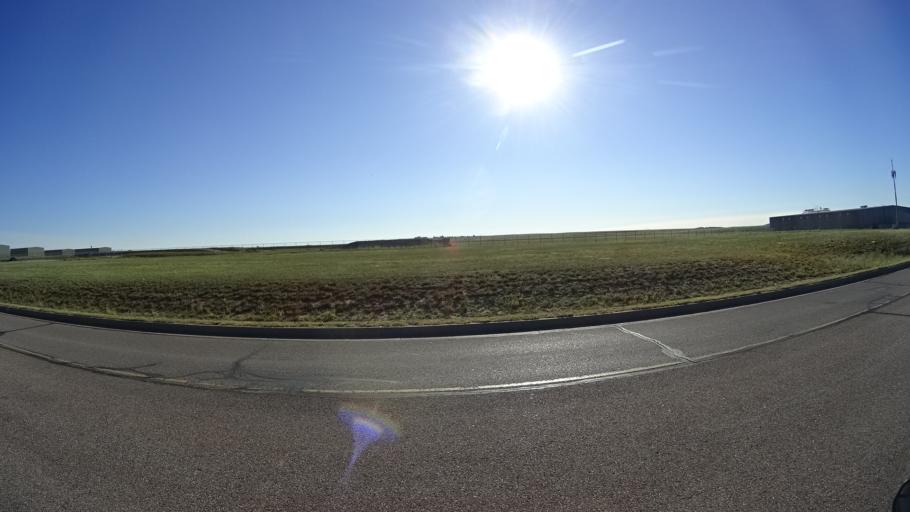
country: US
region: Colorado
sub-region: El Paso County
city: Security-Widefield
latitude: 38.7970
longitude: -104.7237
